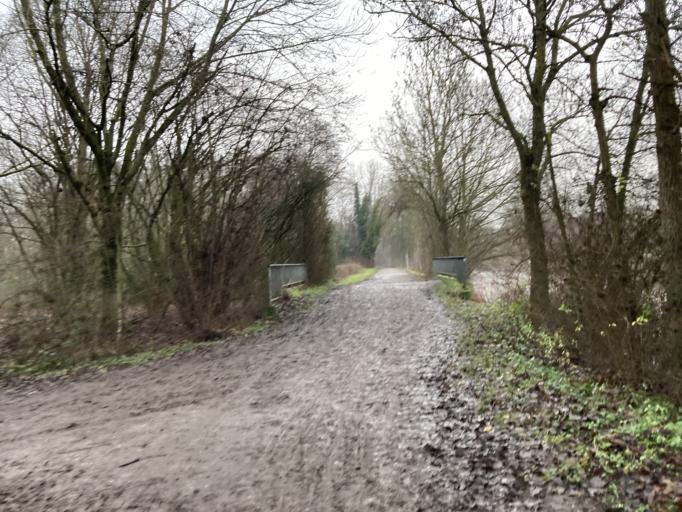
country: DE
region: North Rhine-Westphalia
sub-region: Regierungsbezirk Dusseldorf
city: Neubrueck
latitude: 51.1226
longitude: 6.6345
